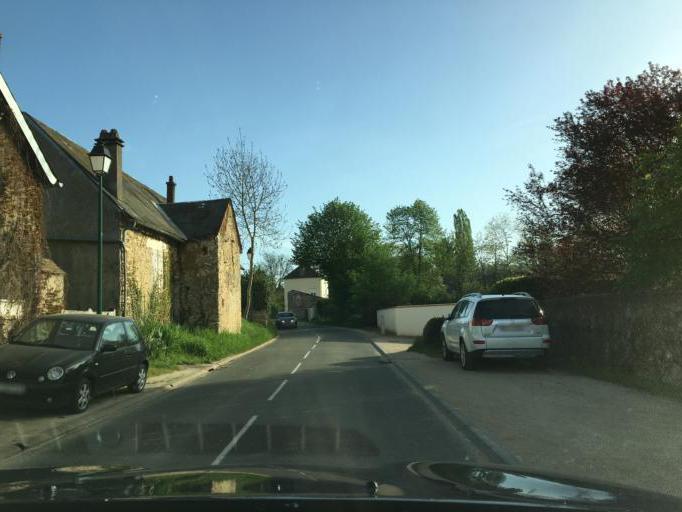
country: FR
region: Centre
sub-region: Departement d'Eure-et-Loir
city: Epernon
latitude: 48.6194
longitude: 1.6764
